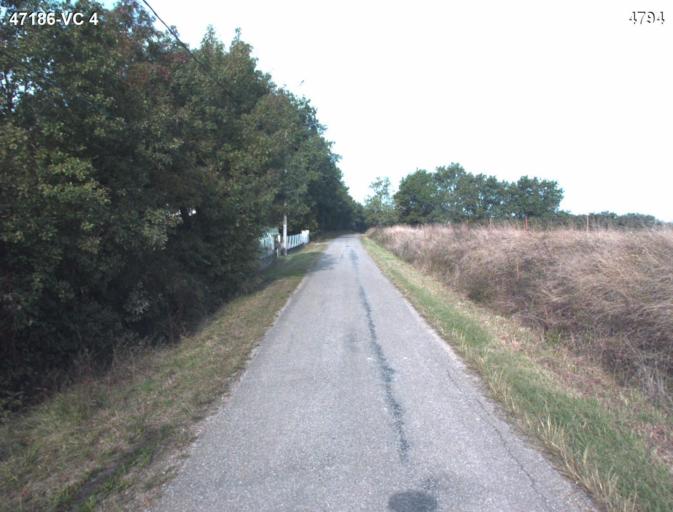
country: FR
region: Aquitaine
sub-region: Departement du Lot-et-Garonne
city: Sainte-Colombe-en-Bruilhois
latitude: 44.1920
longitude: 0.4551
